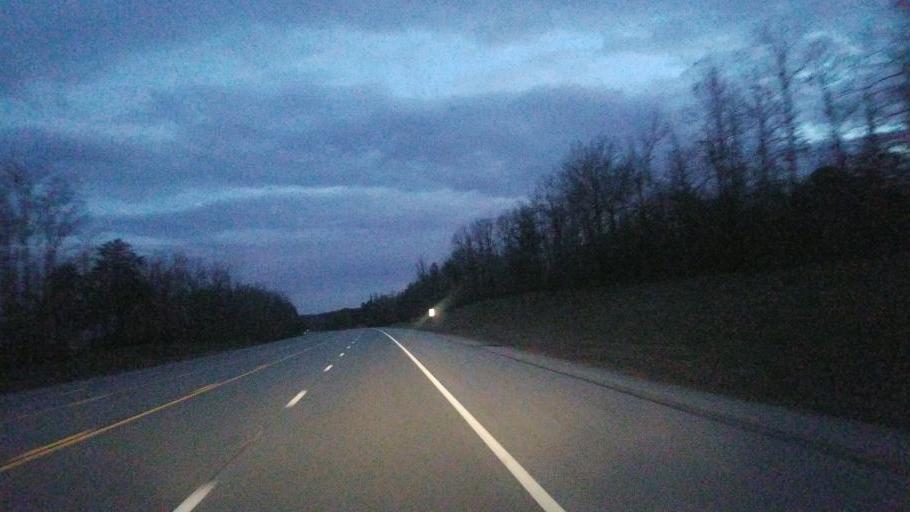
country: US
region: Tennessee
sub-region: Sequatchie County
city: Dunlap
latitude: 35.5352
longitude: -85.4684
